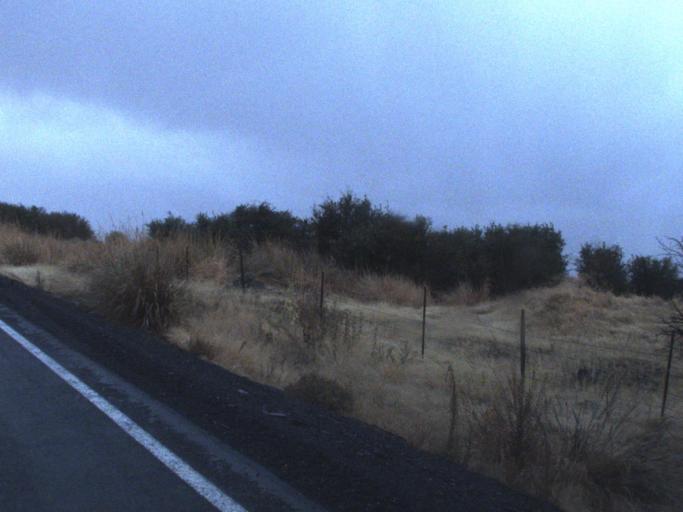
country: US
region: Washington
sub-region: Spokane County
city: Cheney
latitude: 47.1189
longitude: -117.7450
